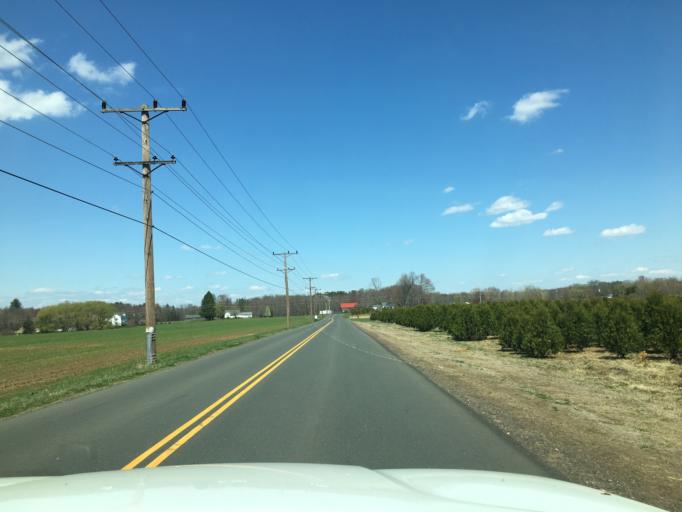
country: US
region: Connecticut
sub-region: Hartford County
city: Hazardville
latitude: 41.9989
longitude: -72.5300
